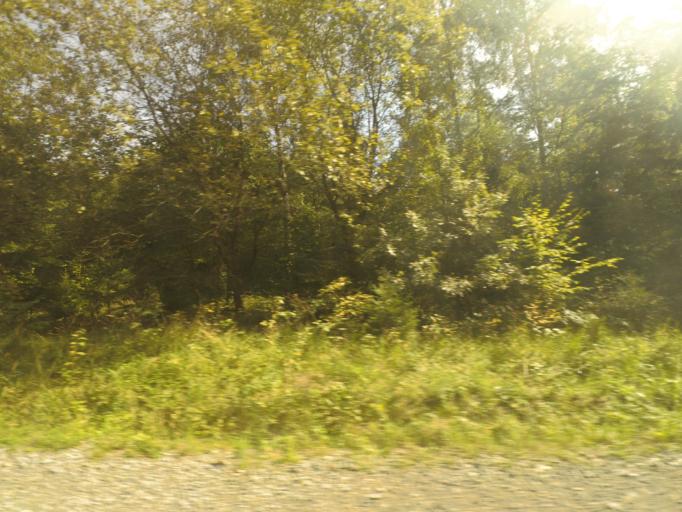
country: DE
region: Thuringia
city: Christes
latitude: 50.6476
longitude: 10.4669
